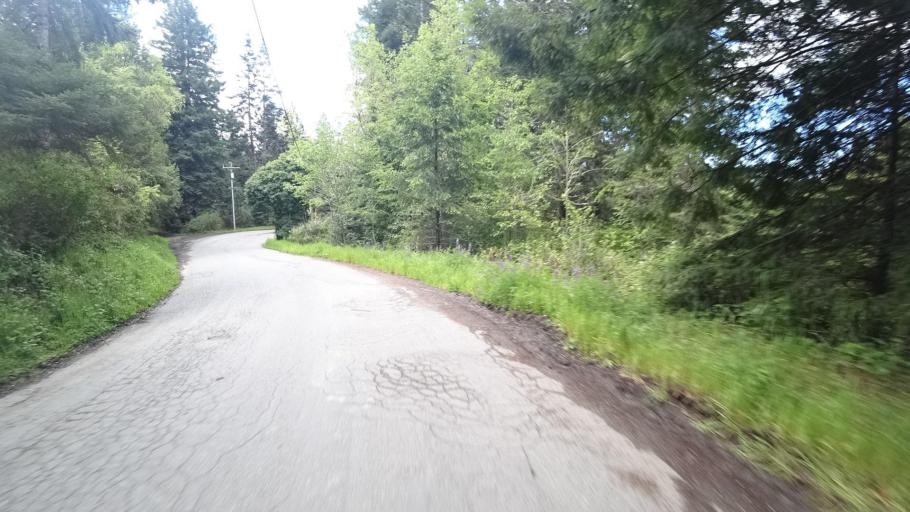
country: US
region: California
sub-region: Humboldt County
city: Blue Lake
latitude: 40.8979
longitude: -124.0005
